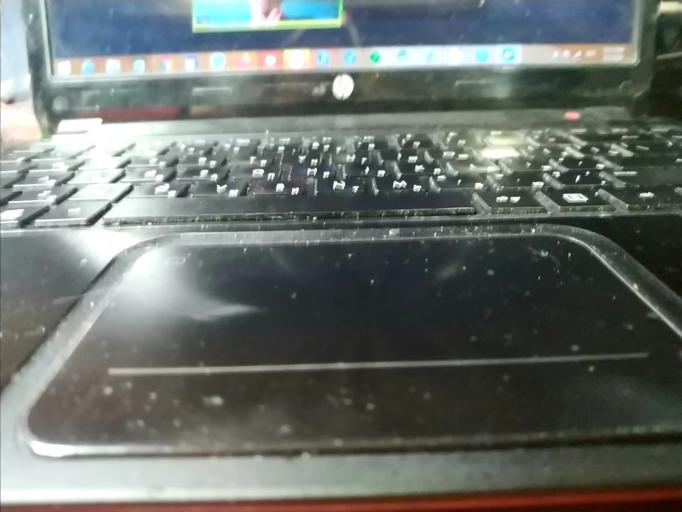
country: RU
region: Tverskaya
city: Ves'yegonsk
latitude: 58.6982
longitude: 37.5439
